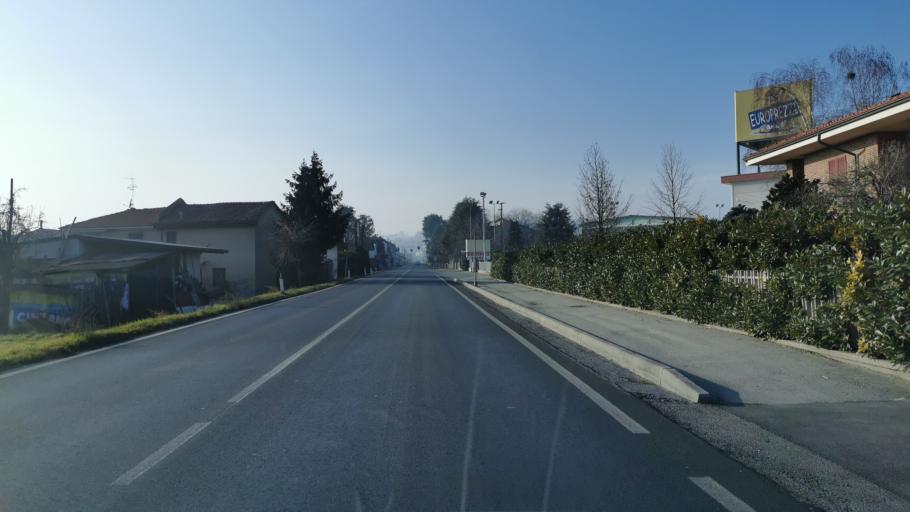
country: IT
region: Piedmont
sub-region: Provincia di Cuneo
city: Pocapaglia
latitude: 44.6967
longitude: 7.8912
